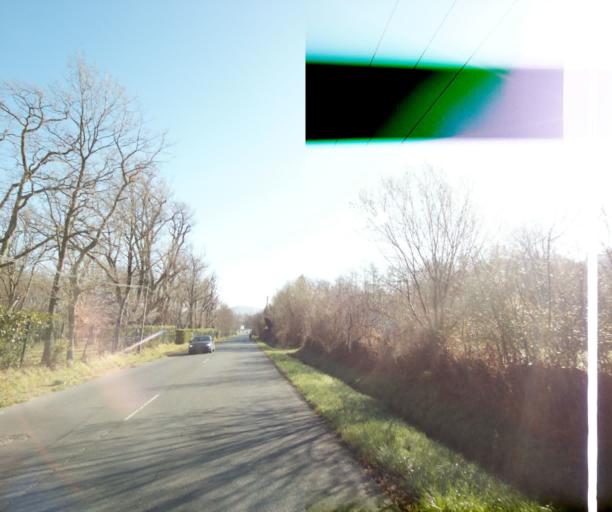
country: FR
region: Aquitaine
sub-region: Departement des Pyrenees-Atlantiques
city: Ascain
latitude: 43.3390
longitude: -1.6489
